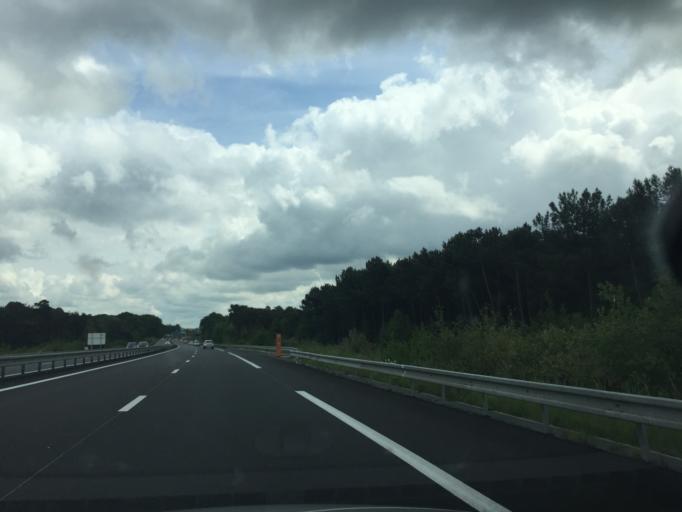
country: FR
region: Pays de la Loire
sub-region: Departement de la Sarthe
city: Change
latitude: 48.0070
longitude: 0.3035
